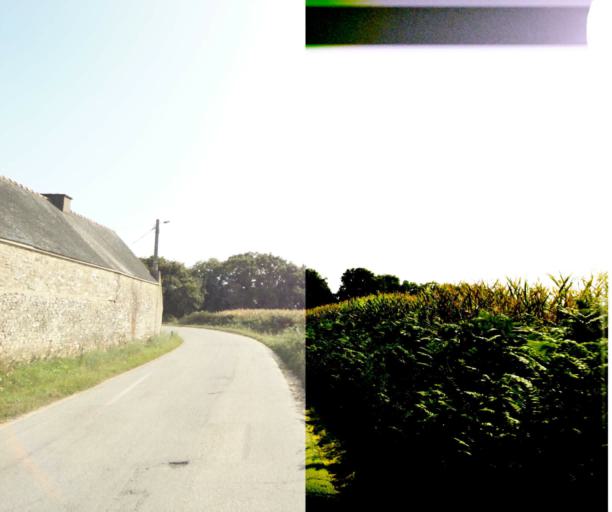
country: FR
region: Brittany
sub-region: Departement du Morbihan
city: Riantec
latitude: 47.7294
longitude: -3.2972
